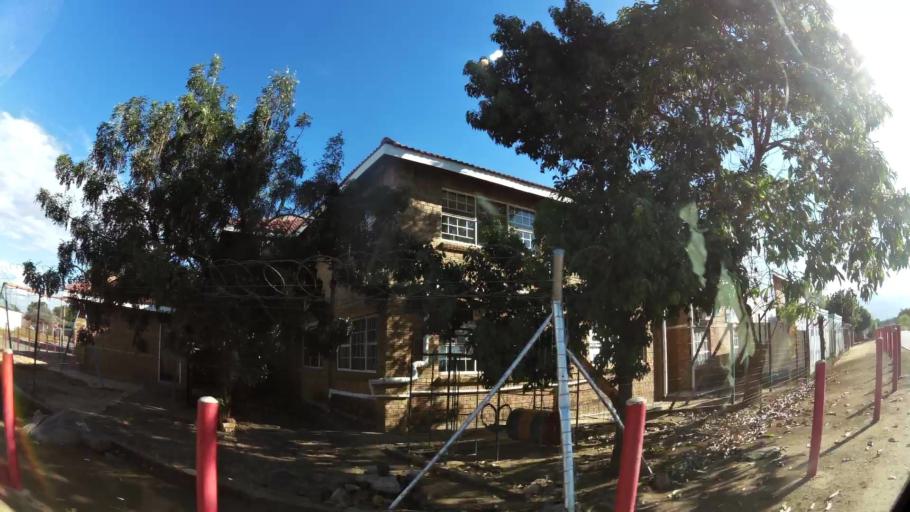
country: ZA
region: Limpopo
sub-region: Waterberg District Municipality
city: Mokopane
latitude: -24.1768
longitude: 28.9990
